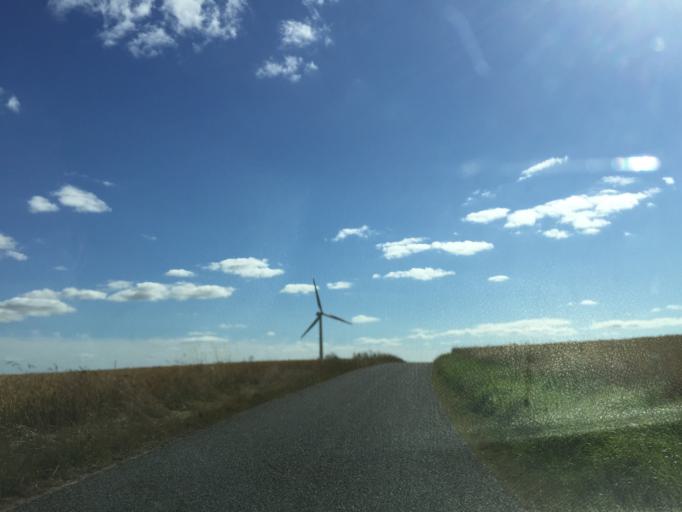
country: DK
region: Central Jutland
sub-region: Viborg Kommune
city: Bjerringbro
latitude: 56.2590
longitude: 9.6895
